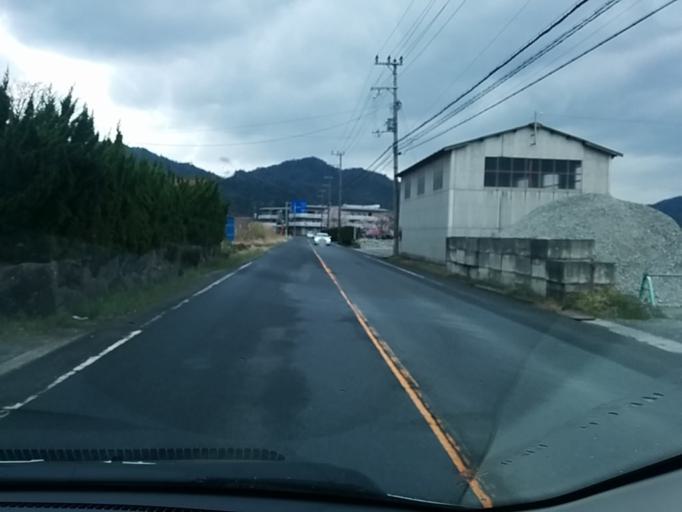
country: JP
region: Kyoto
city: Miyazu
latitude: 35.5548
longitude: 135.1616
